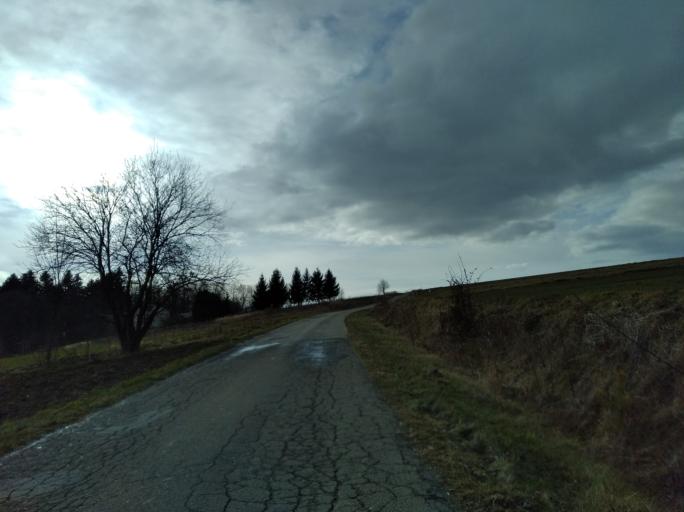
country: PL
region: Subcarpathian Voivodeship
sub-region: Powiat strzyzowski
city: Strzyzow
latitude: 49.8572
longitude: 21.7743
